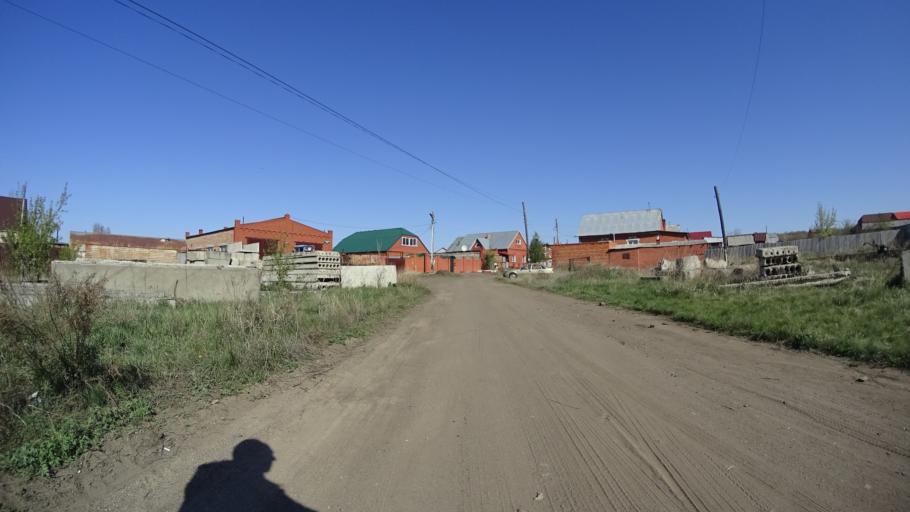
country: RU
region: Chelyabinsk
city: Troitsk
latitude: 54.0964
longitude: 61.5973
